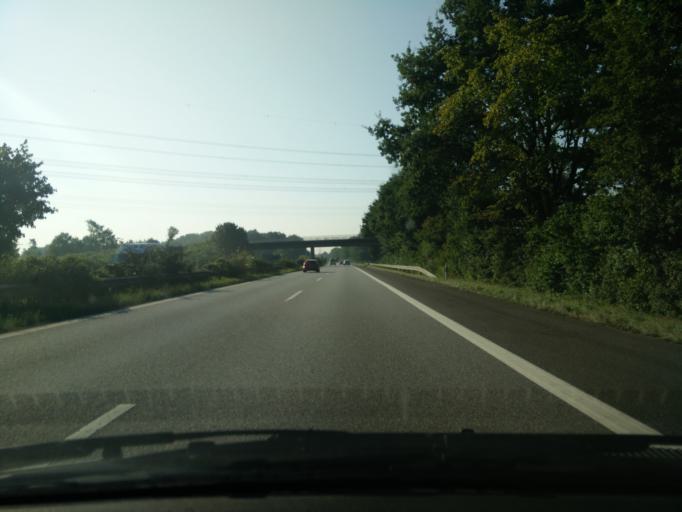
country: DE
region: Schleswig-Holstein
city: Kummerfeld
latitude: 53.7000
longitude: 9.7757
